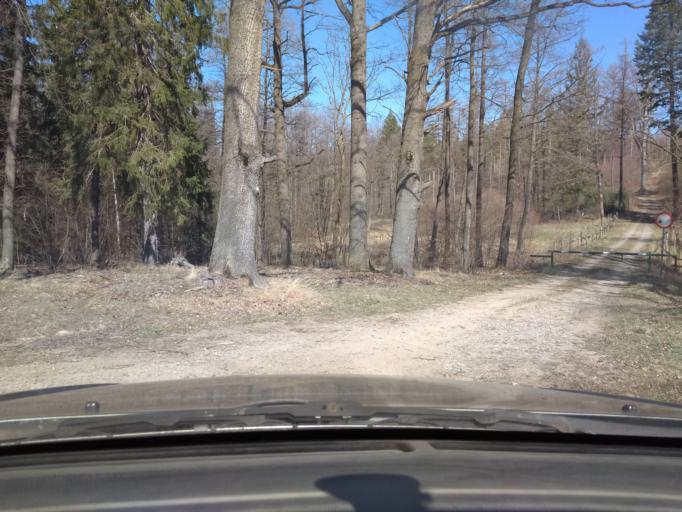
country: PL
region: Lower Silesian Voivodeship
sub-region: Powiat jeleniogorski
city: Sosnowka
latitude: 50.8366
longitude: 15.7429
